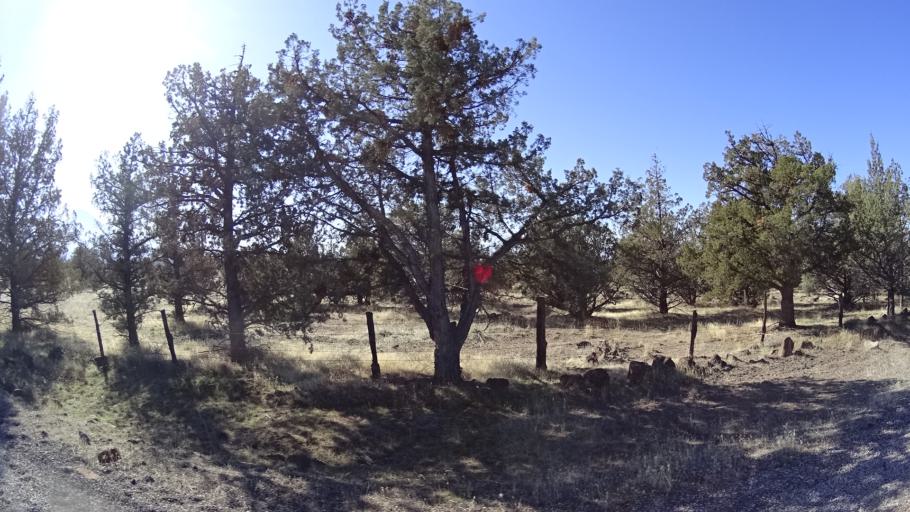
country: US
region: California
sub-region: Siskiyou County
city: Weed
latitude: 41.6030
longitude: -122.3057
